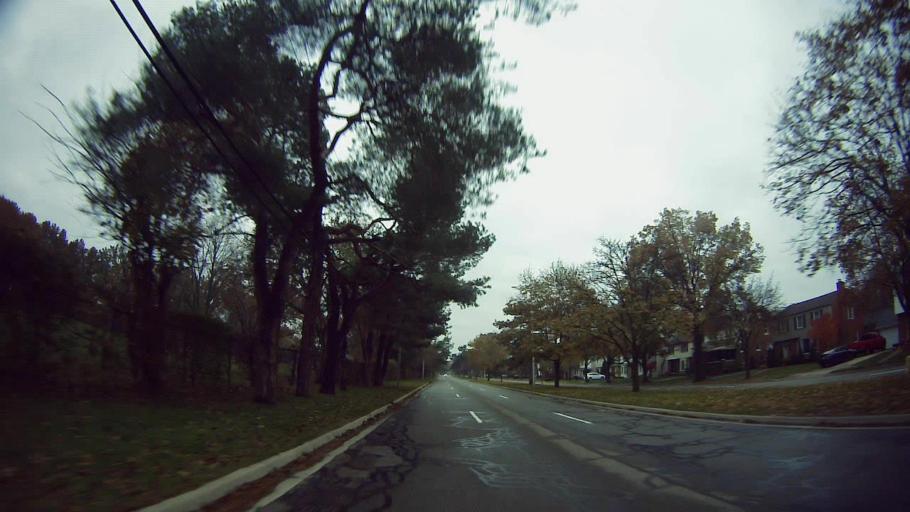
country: US
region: Michigan
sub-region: Wayne County
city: Dearborn Heights
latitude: 42.3154
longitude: -83.2544
